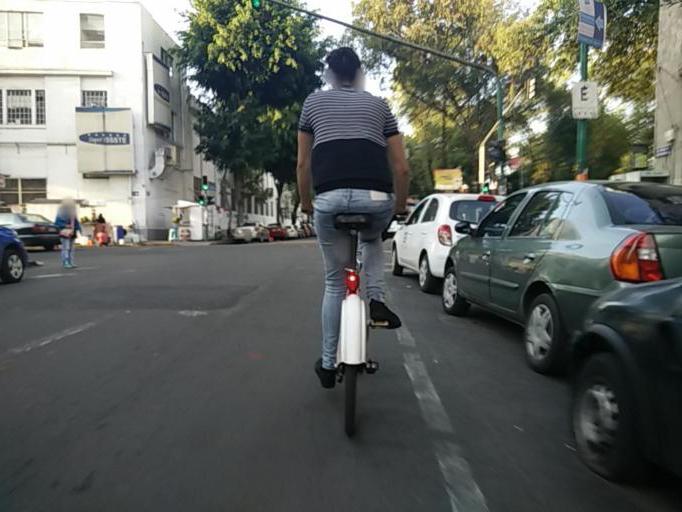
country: MX
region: Mexico City
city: Cuauhtemoc
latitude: 19.4272
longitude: -99.1508
